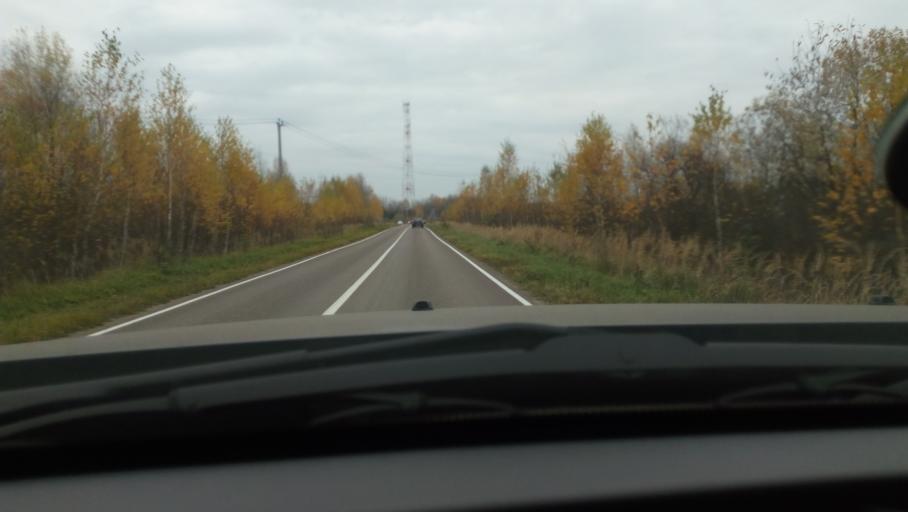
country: RU
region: Moskovskaya
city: Avsyunino
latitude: 55.5966
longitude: 39.2421
